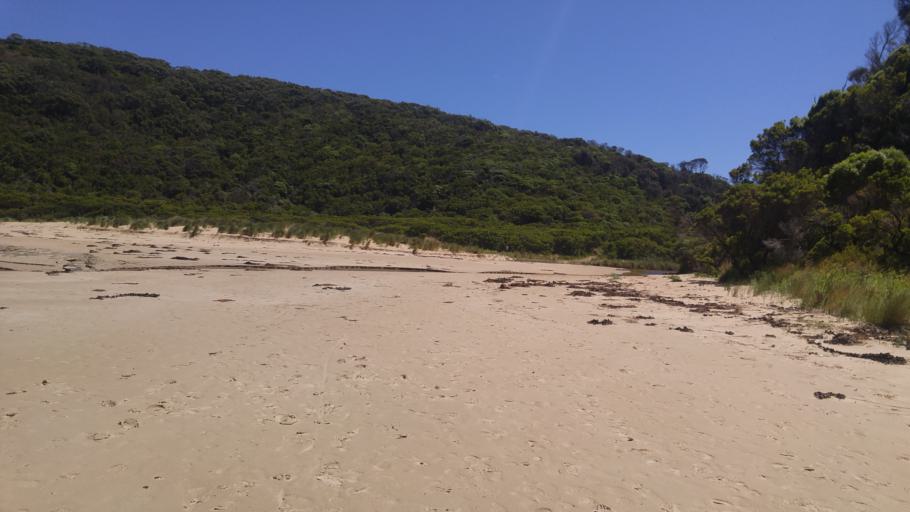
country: AU
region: Victoria
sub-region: Colac-Otway
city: Apollo Bay
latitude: -38.8446
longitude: 143.5616
